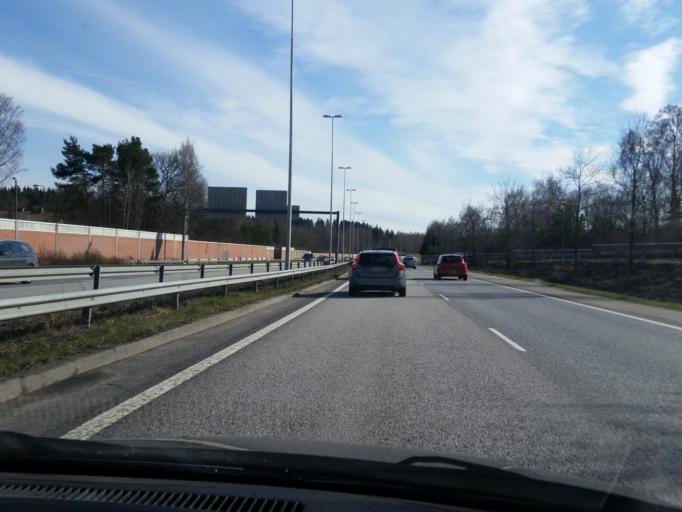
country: FI
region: Uusimaa
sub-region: Helsinki
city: Helsinki
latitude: 60.2421
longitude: 24.9476
